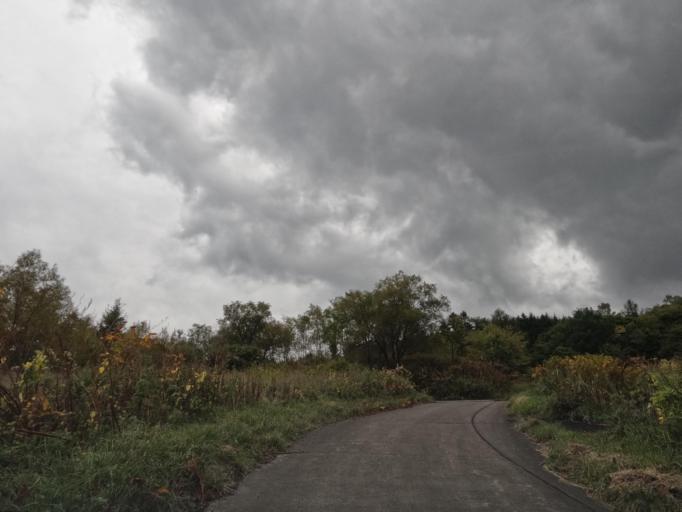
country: JP
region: Hokkaido
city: Date
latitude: 42.5060
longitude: 140.9061
